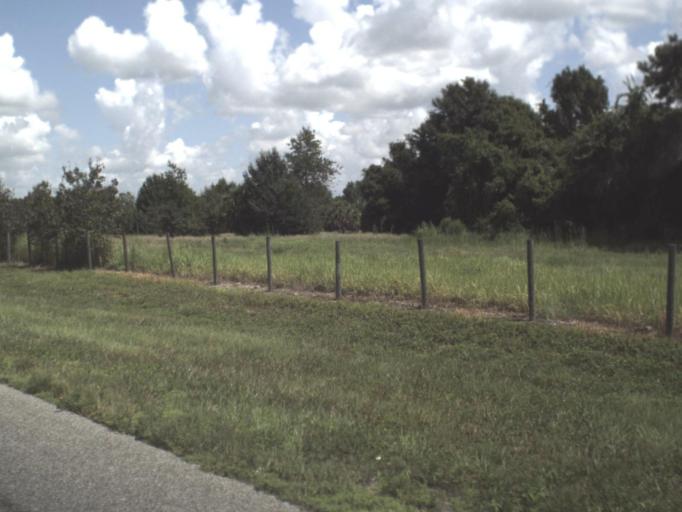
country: US
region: Florida
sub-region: Hardee County
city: Zolfo Springs
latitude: 27.5162
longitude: -81.8043
